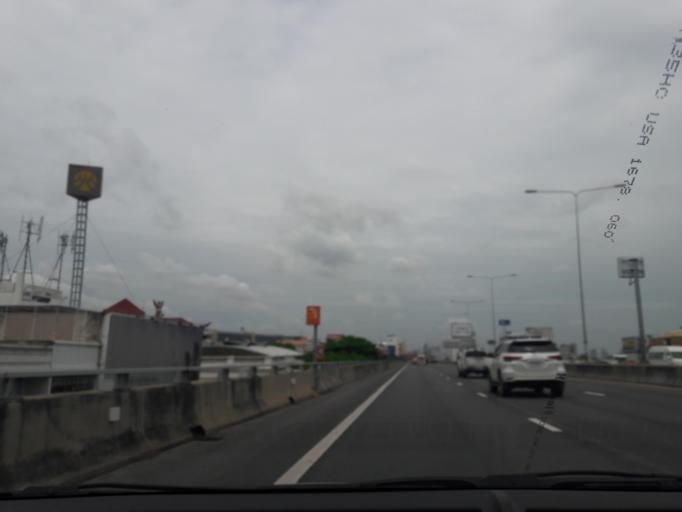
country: TH
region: Bangkok
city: Suan Luang
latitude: 13.7421
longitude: 100.6326
